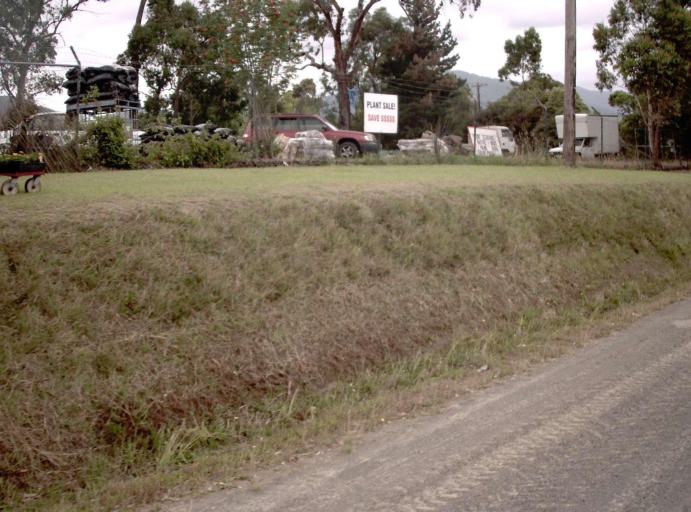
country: AU
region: Victoria
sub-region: Yarra Ranges
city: Launching Place
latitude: -37.7801
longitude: 145.5680
